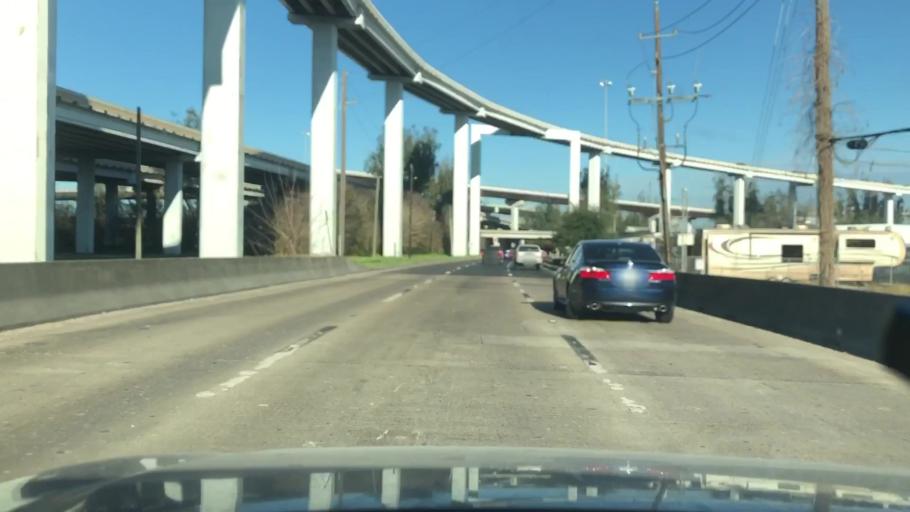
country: US
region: Texas
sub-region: Fort Bend County
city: Meadows Place
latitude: 29.6589
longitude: -95.5556
